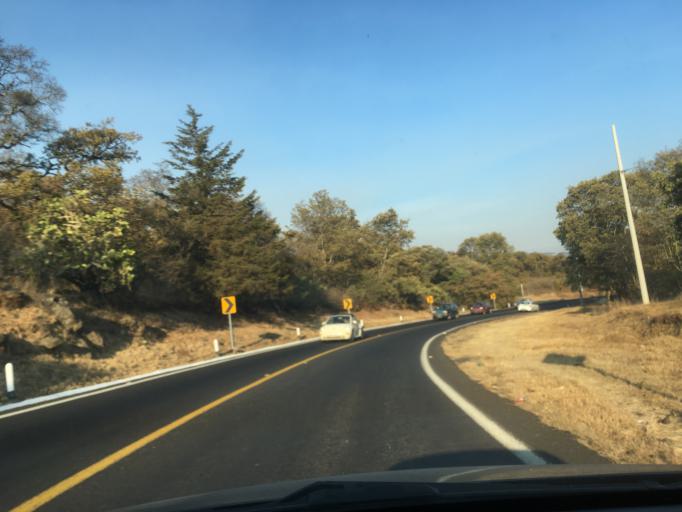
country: MX
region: Michoacan
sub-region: Morelia
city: Iratzio
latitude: 19.6306
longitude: -101.4421
